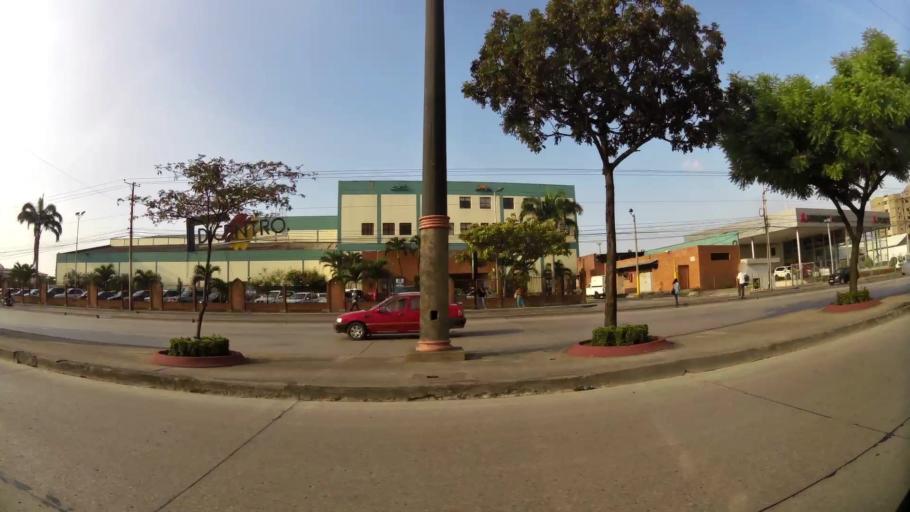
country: EC
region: Guayas
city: Eloy Alfaro
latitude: -2.1508
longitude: -79.8992
